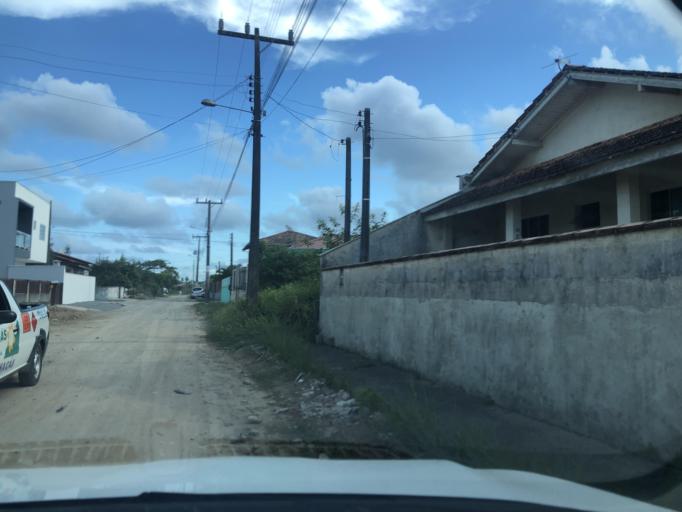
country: BR
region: Santa Catarina
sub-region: Sao Francisco Do Sul
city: Sao Francisco do Sul
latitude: -26.2212
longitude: -48.5248
